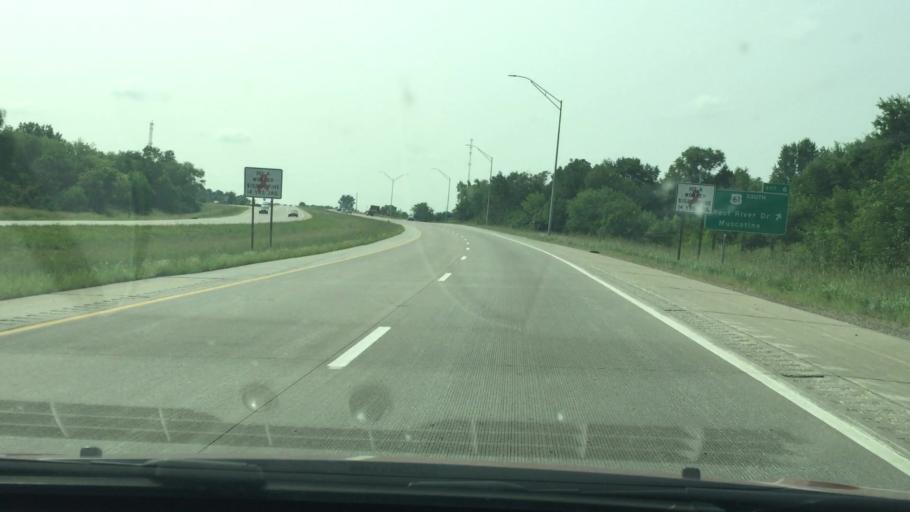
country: US
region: Iowa
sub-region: Scott County
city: Buffalo
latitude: 41.5151
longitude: -90.6747
